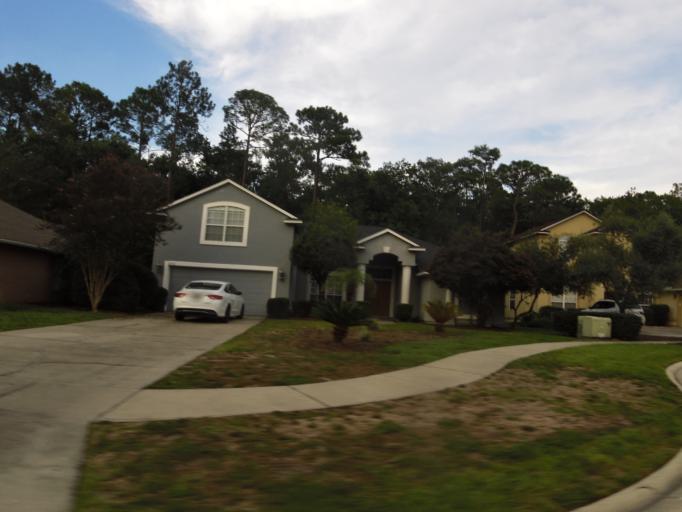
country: US
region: Florida
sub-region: Saint Johns County
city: Palm Valley
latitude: 30.2089
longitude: -81.5192
